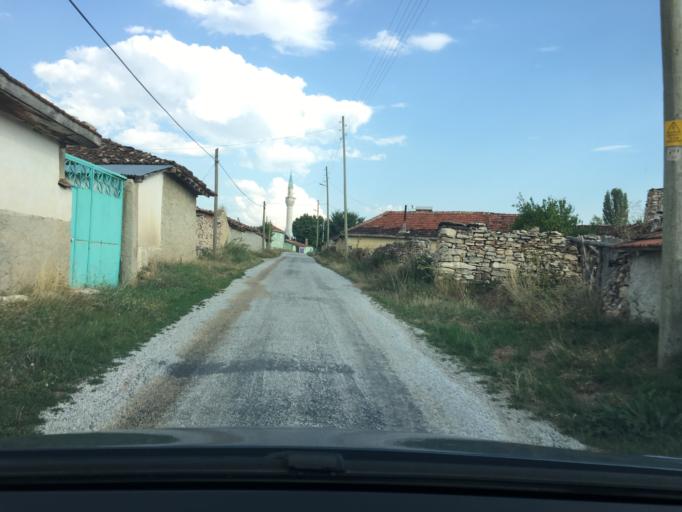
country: TR
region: Eskisehir
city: Kirka
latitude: 39.2776
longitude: 30.6756
